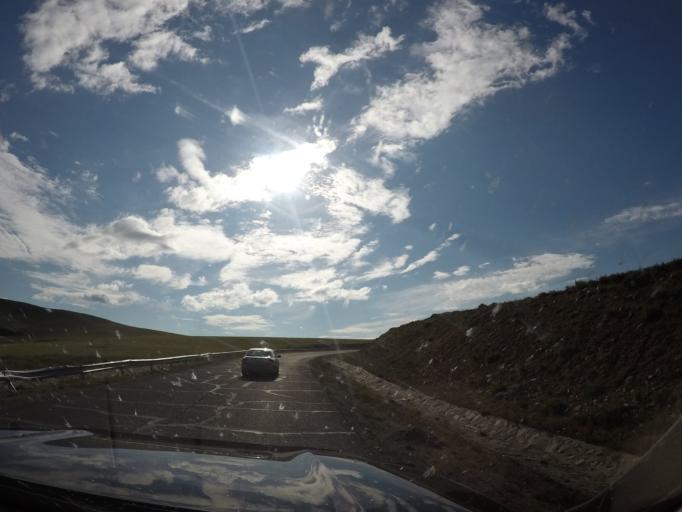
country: MN
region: Hentiy
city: Modot
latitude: 47.7939
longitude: 108.7663
